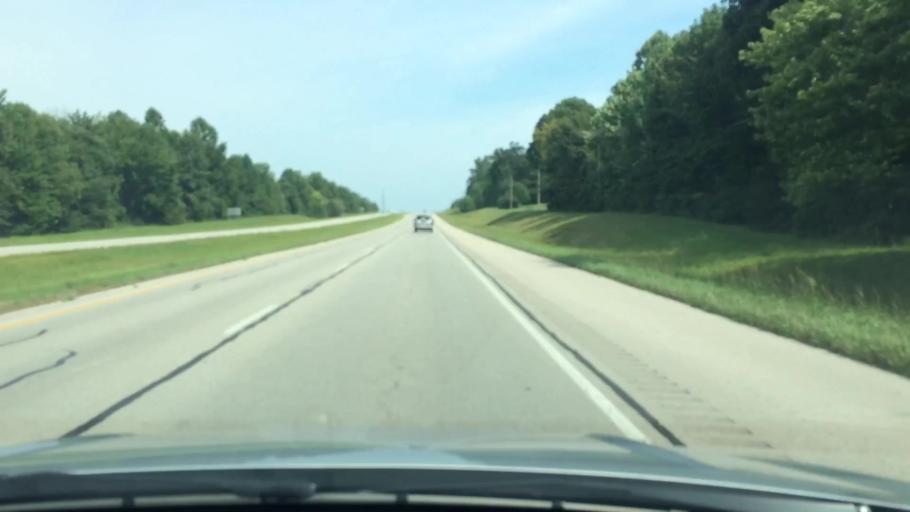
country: US
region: Kentucky
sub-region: Anderson County
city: Lawrenceburg
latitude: 38.0792
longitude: -84.9174
